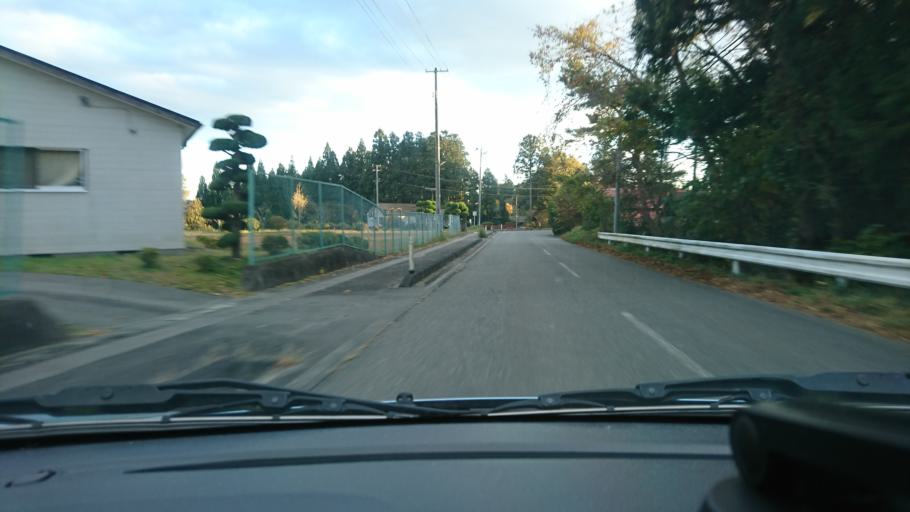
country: JP
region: Iwate
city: Ichinoseki
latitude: 38.7974
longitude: 141.1927
